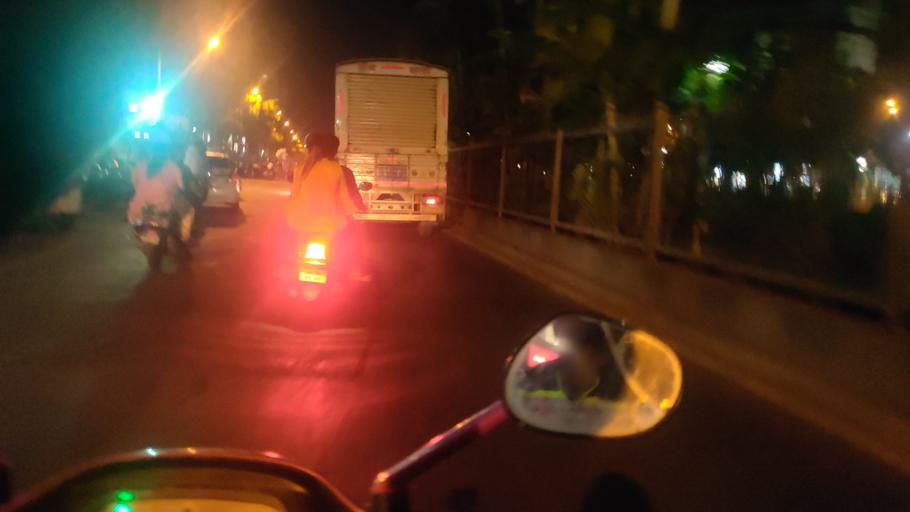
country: IN
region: Maharashtra
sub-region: Thane
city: Bhayandar
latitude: 19.2947
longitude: 72.8487
